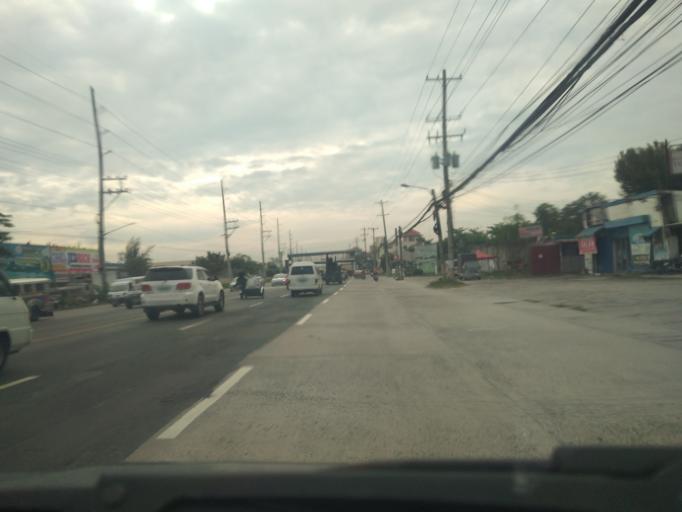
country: PH
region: Central Luzon
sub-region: Province of Pampanga
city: Magliman
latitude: 15.0541
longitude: 120.6612
